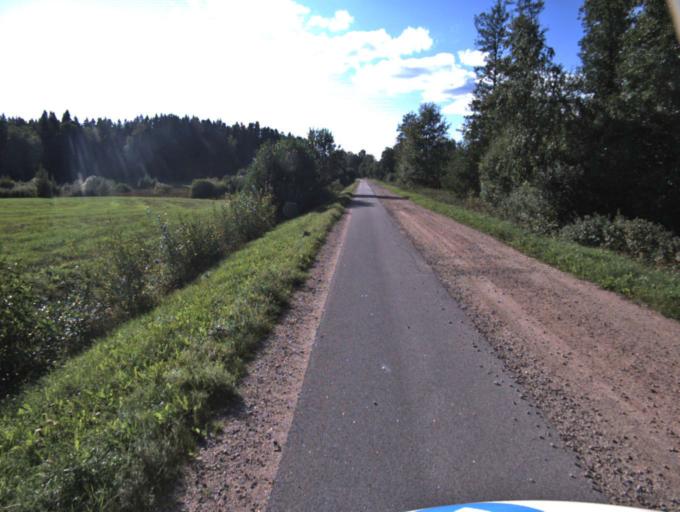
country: SE
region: Vaestra Goetaland
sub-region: Boras Kommun
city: Dalsjofors
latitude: 57.8250
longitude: 13.1672
